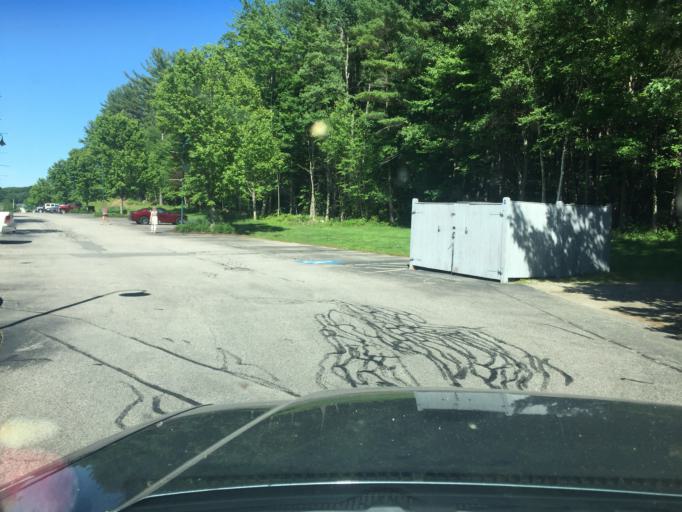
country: US
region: Maine
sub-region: York County
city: York Harbor
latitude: 43.1538
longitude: -70.6577
